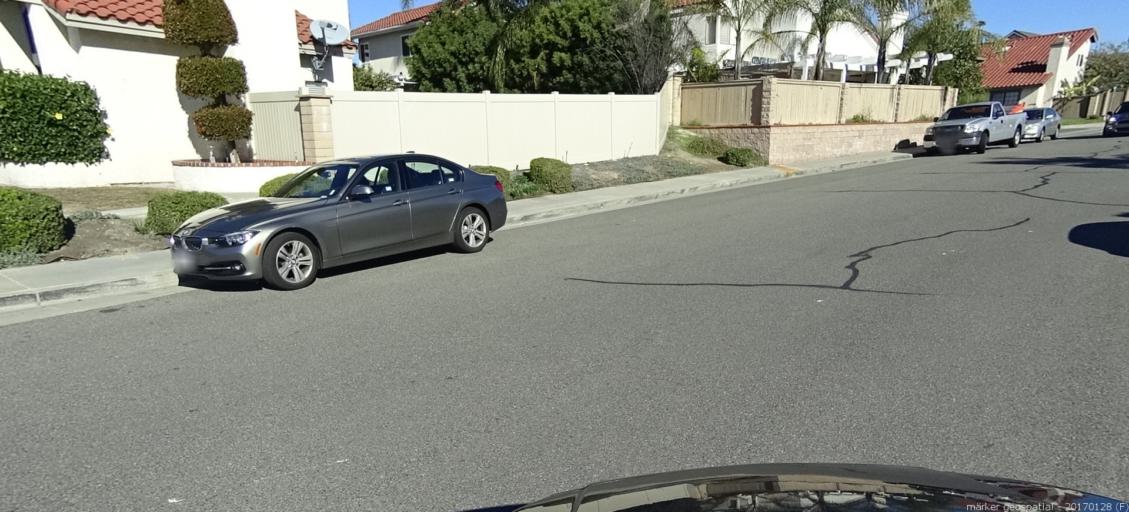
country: US
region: California
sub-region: Orange County
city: Lake Forest
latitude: 33.6514
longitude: -117.6774
